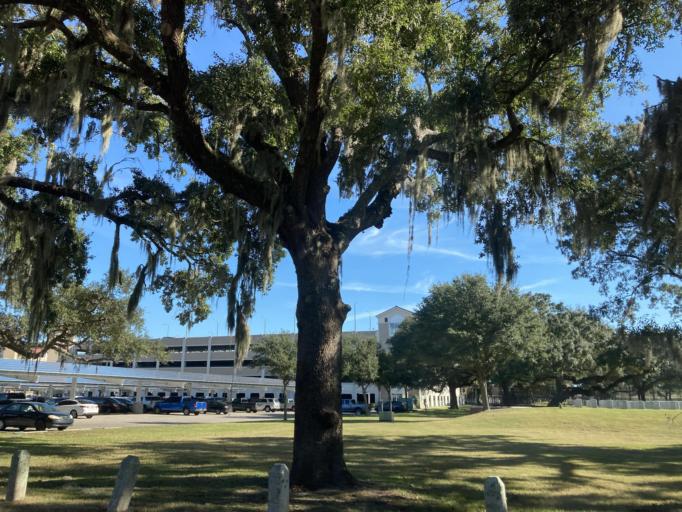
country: US
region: Mississippi
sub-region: Harrison County
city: D'Iberville
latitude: 30.4128
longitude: -88.9436
